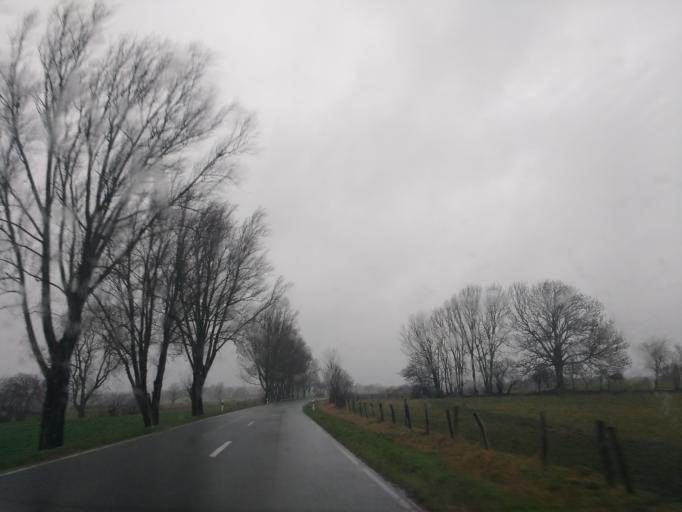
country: DE
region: Schleswig-Holstein
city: Blekendorf
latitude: 54.2989
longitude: 10.6615
